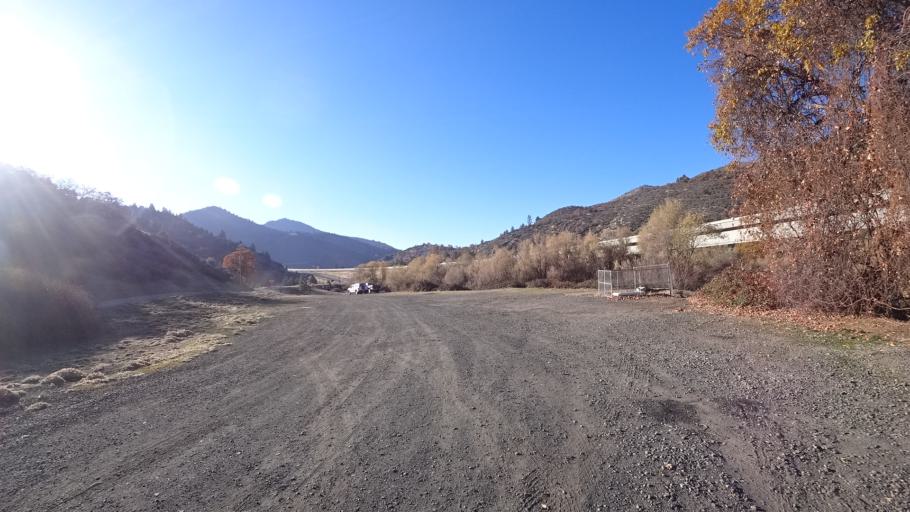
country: US
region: California
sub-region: Siskiyou County
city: Montague
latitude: 41.8565
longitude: -122.5707
